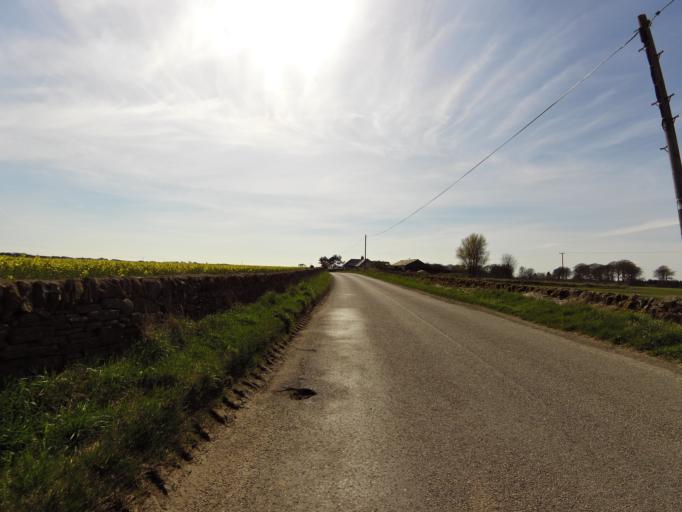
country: GB
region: Scotland
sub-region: Angus
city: Arbroath
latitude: 56.5963
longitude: -2.5505
